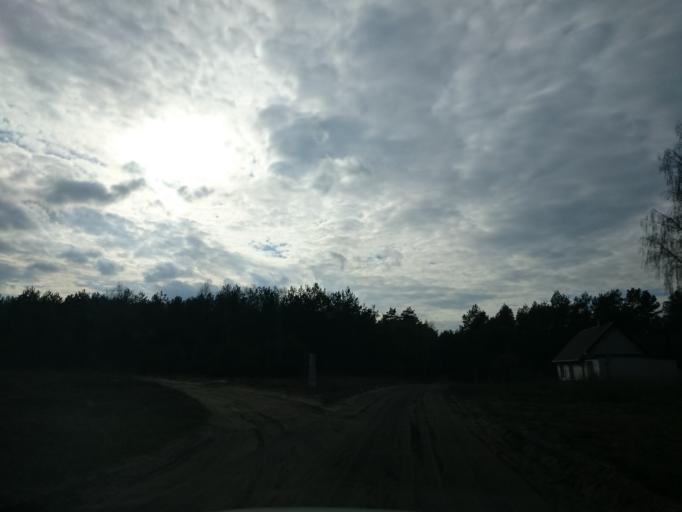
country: PL
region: Kujawsko-Pomorskie
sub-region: Powiat golubsko-dobrzynski
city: Ciechocin
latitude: 53.0494
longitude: 18.8688
